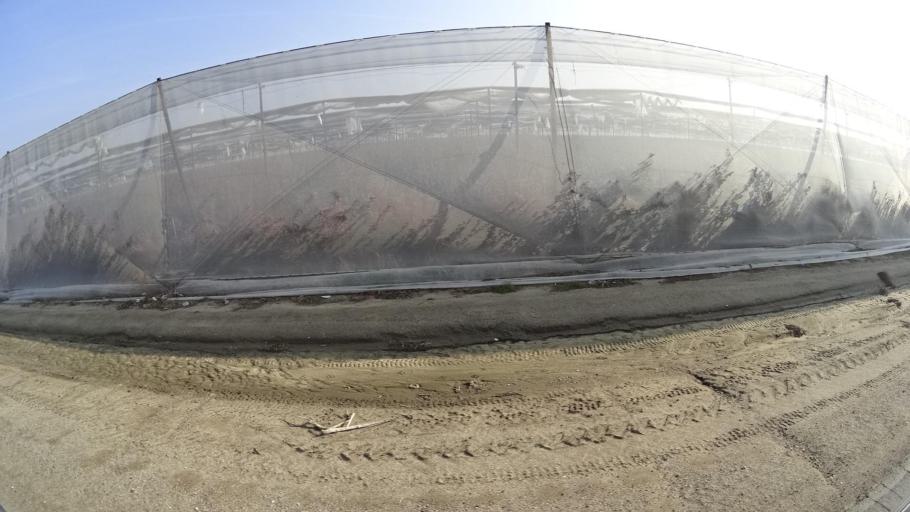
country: US
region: California
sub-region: Kern County
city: Arvin
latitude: 35.0482
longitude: -118.8466
